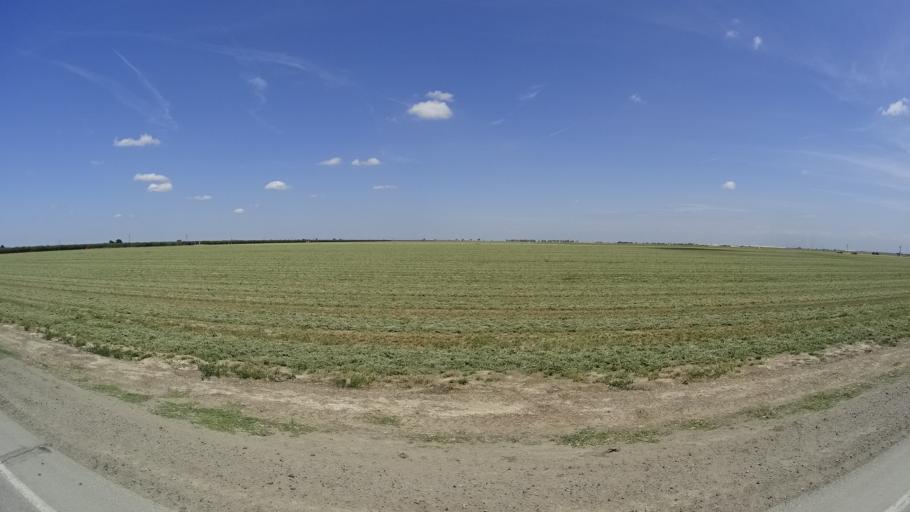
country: US
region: California
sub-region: Kings County
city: Home Garden
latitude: 36.2989
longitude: -119.5391
